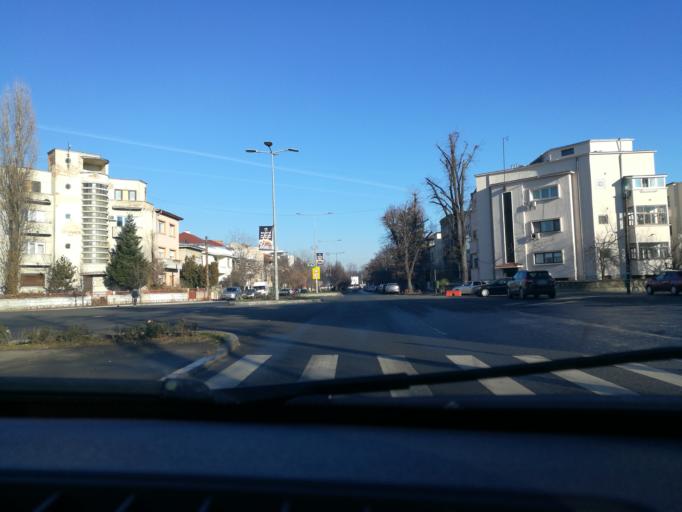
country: RO
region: Bucuresti
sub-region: Municipiul Bucuresti
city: Bucuresti
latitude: 44.4671
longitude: 26.0703
